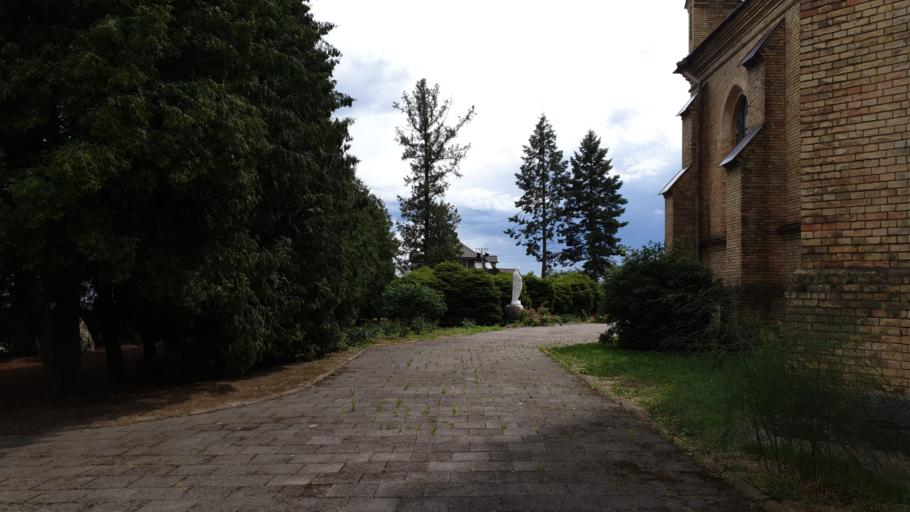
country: LT
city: Skaidiskes
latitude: 54.6974
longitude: 25.4110
